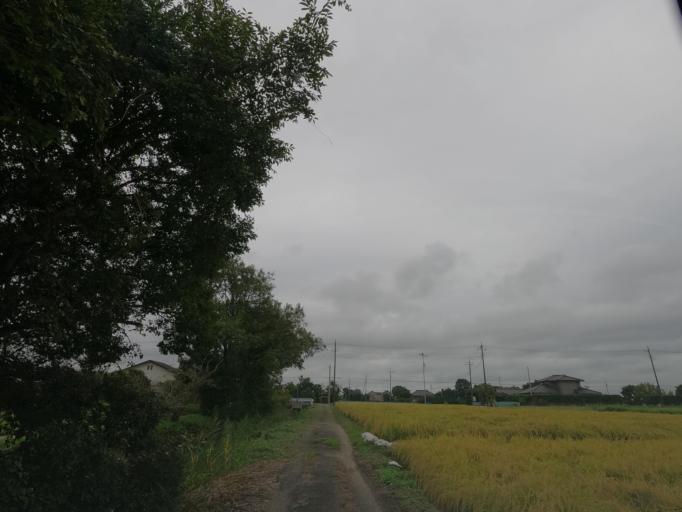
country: JP
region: Ibaraki
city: Toride
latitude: 35.9242
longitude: 140.0715
